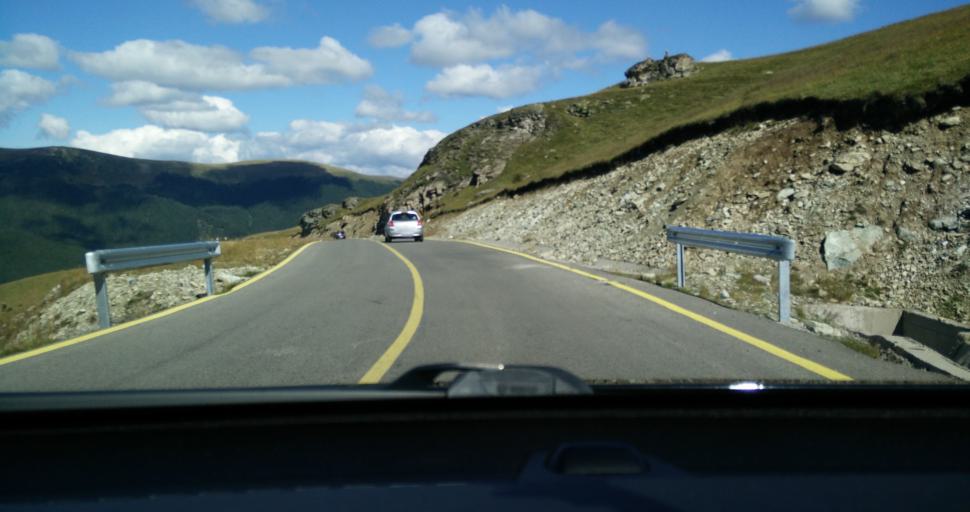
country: RO
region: Gorj
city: Novaci-Straini
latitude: 45.3788
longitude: 23.6463
